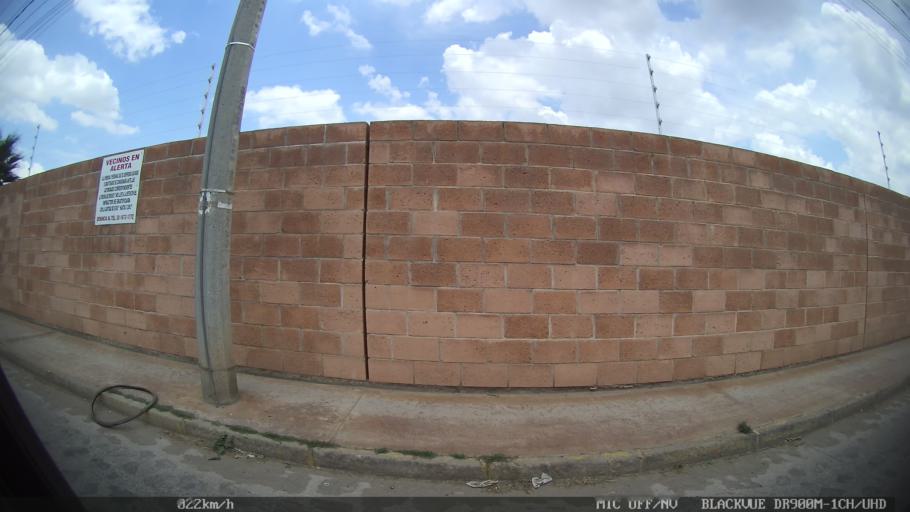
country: MX
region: Jalisco
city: Tonala
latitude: 20.6671
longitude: -103.2286
